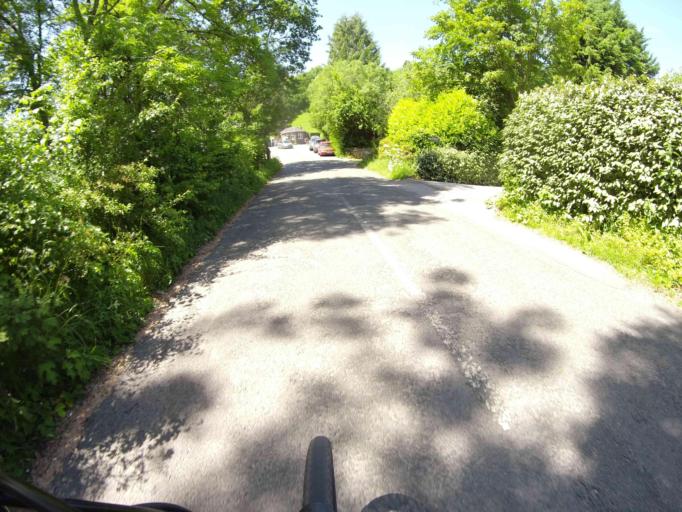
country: GB
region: England
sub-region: Devon
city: Bovey Tracey
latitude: 50.6206
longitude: -3.7169
